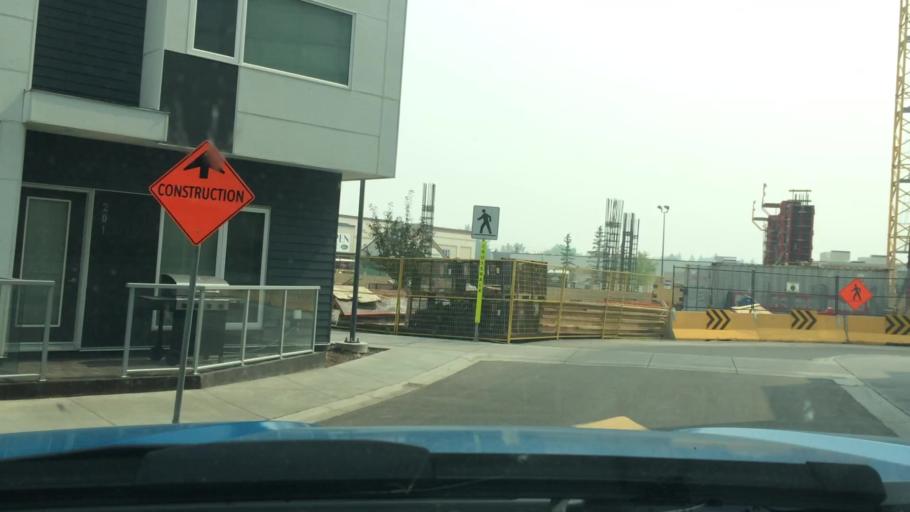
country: CA
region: Alberta
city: Calgary
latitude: 51.0871
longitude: -114.1281
